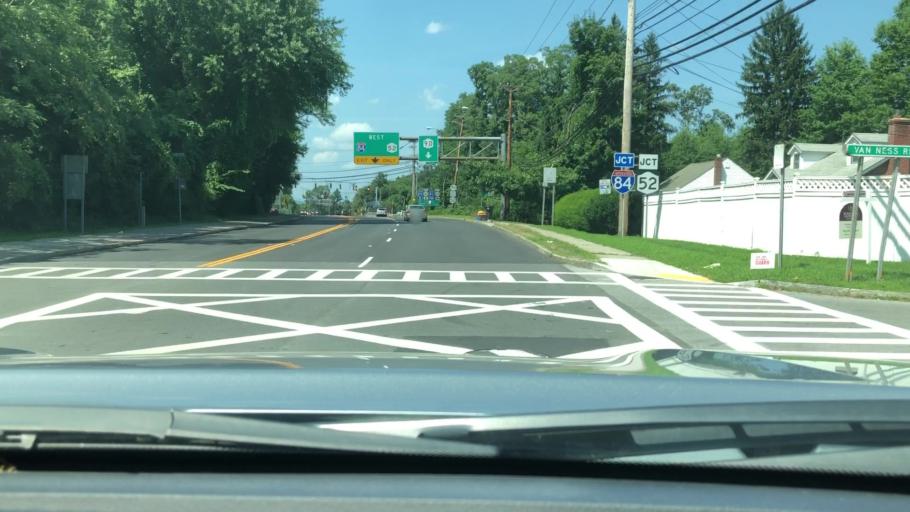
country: US
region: New York
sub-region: Dutchess County
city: Beacon
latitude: 41.5160
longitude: -73.9731
